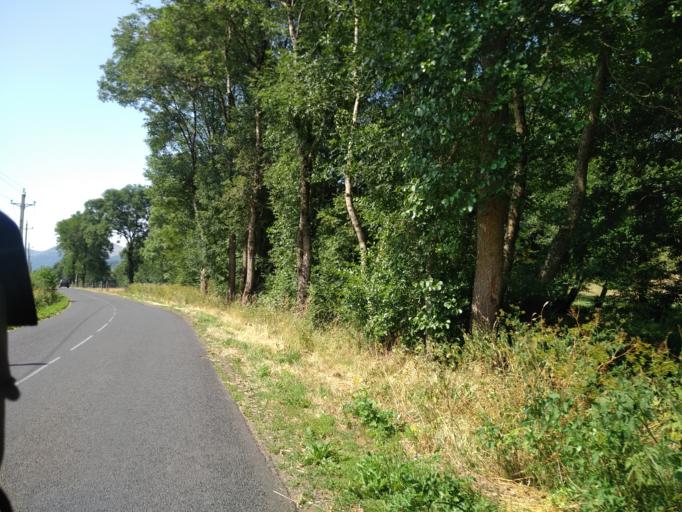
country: FR
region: Auvergne
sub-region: Departement du Cantal
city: Riom-es-Montagnes
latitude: 45.1763
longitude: 2.7184
